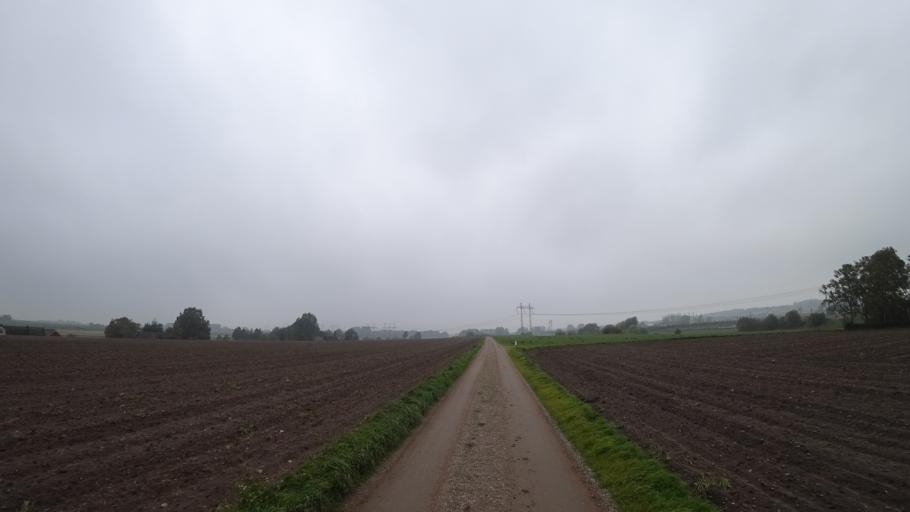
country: SE
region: Skane
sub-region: Kavlinge Kommun
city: Kaevlinge
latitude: 55.8148
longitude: 13.0861
